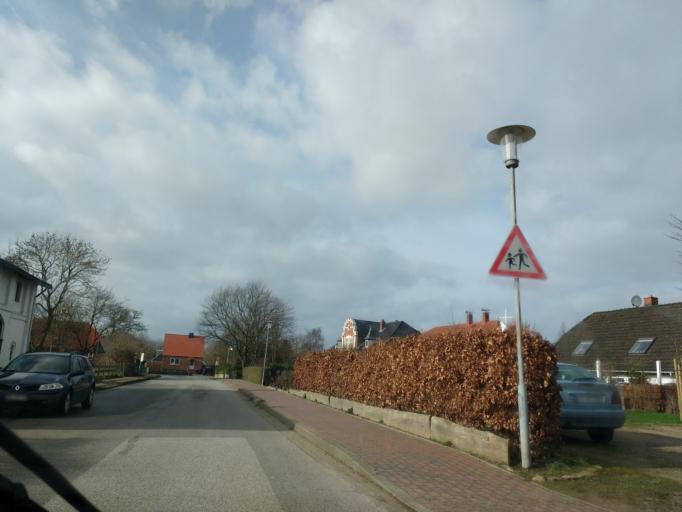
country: DE
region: Schleswig-Holstein
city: Grossenbrode
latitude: 54.3746
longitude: 11.0867
